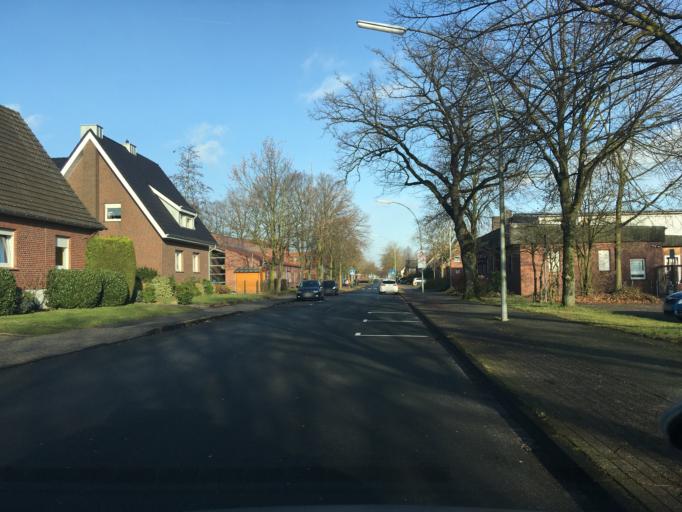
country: DE
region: North Rhine-Westphalia
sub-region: Regierungsbezirk Munster
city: Gescher
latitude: 51.9488
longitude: 6.9904
